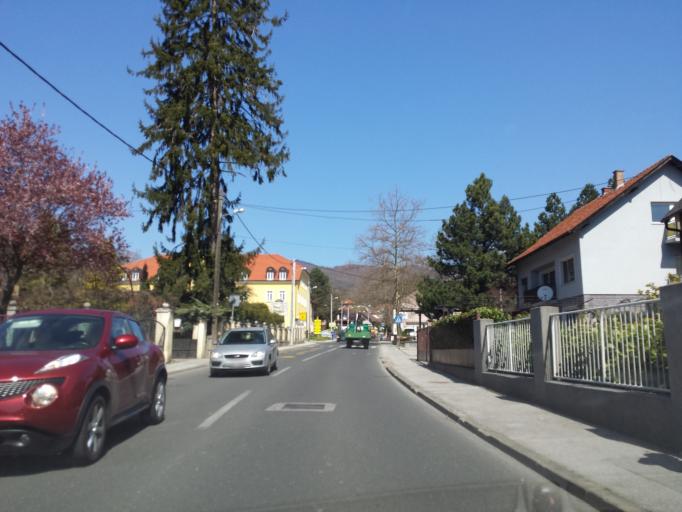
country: HR
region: Grad Zagreb
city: Zagreb
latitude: 45.8502
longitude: 15.9755
